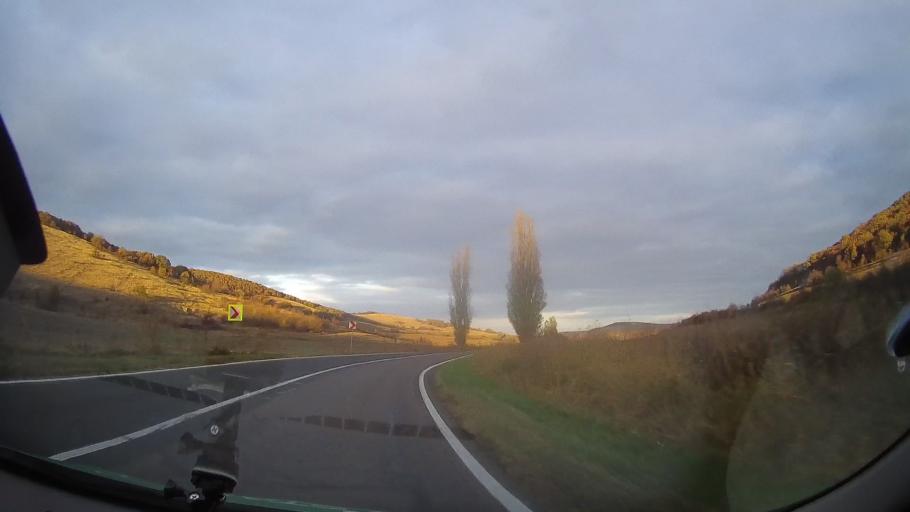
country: RO
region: Tulcea
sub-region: Comuna Ciucurova
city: Ciucurova
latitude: 44.9613
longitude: 28.5200
